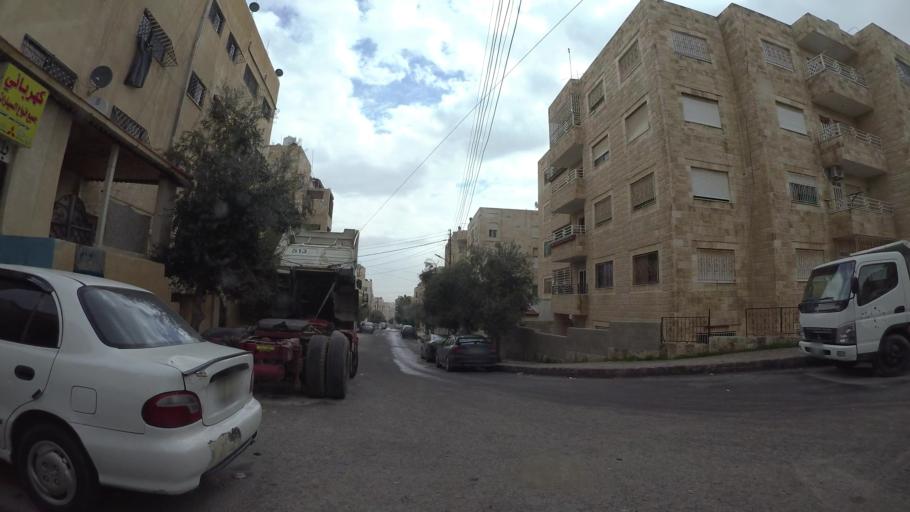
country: JO
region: Amman
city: Amman
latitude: 31.9868
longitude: 35.9249
